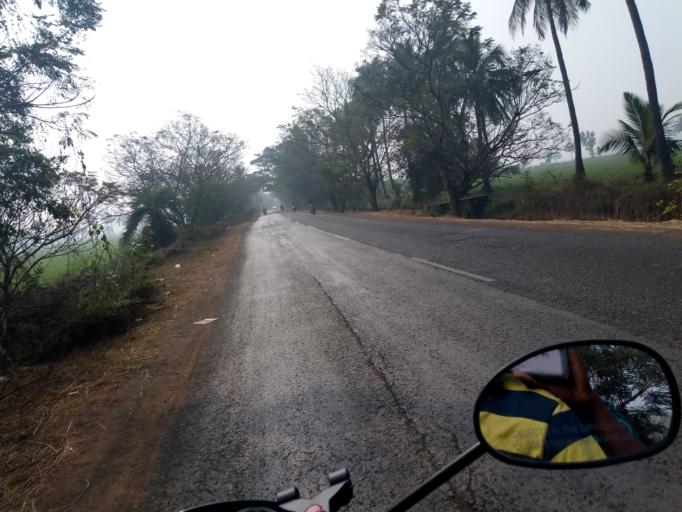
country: IN
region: Andhra Pradesh
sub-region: West Godavari
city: Tadepallegudem
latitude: 16.8063
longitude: 81.4098
